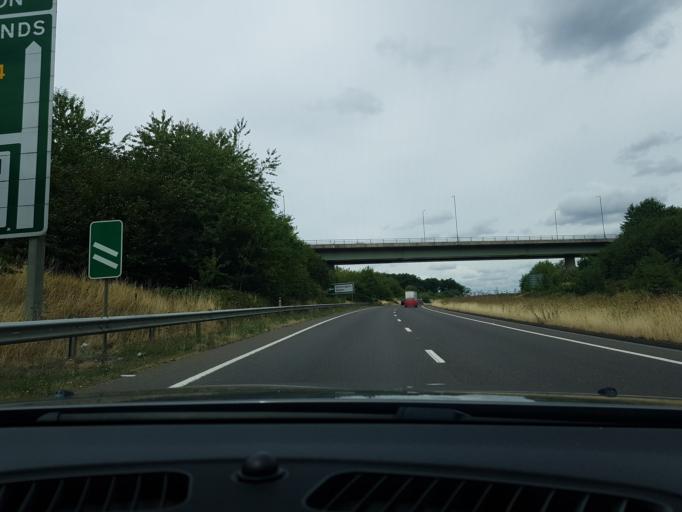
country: GB
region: England
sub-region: West Berkshire
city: Newbury
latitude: 51.4090
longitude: -1.3553
